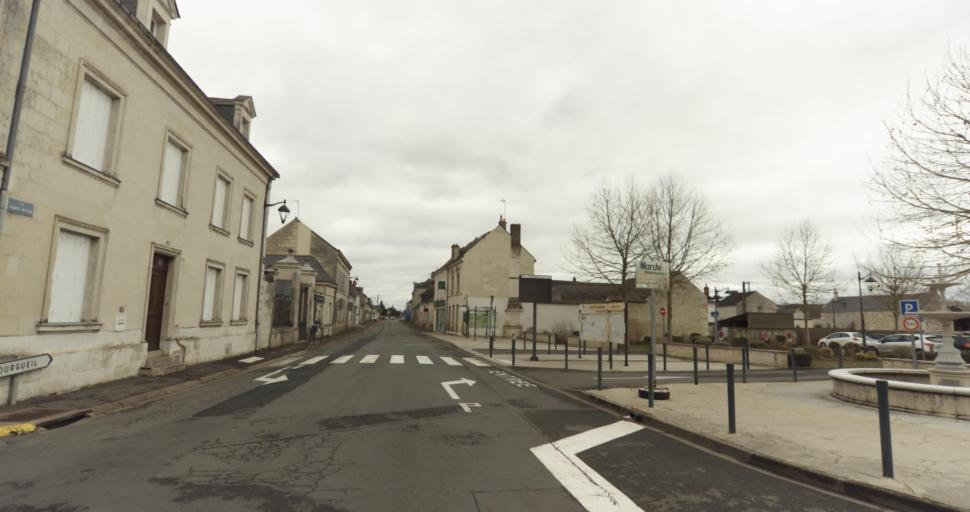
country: FR
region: Pays de la Loire
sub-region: Departement de Maine-et-Loire
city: Allonnes
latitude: 47.2931
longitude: 0.0241
